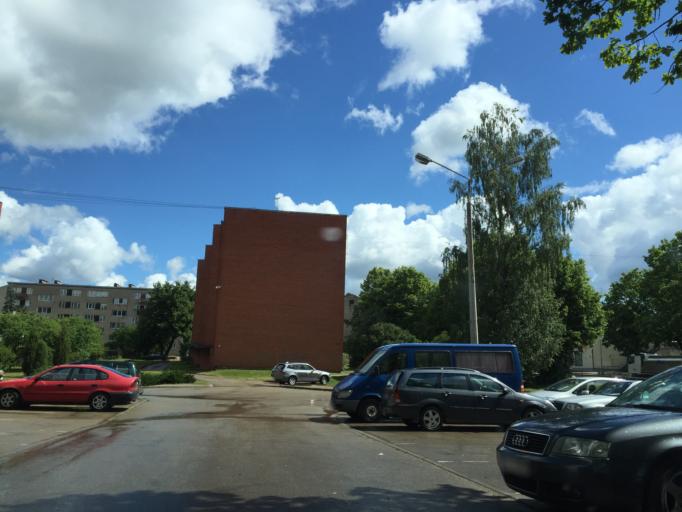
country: LV
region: Lecava
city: Iecava
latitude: 56.5961
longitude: 24.1923
